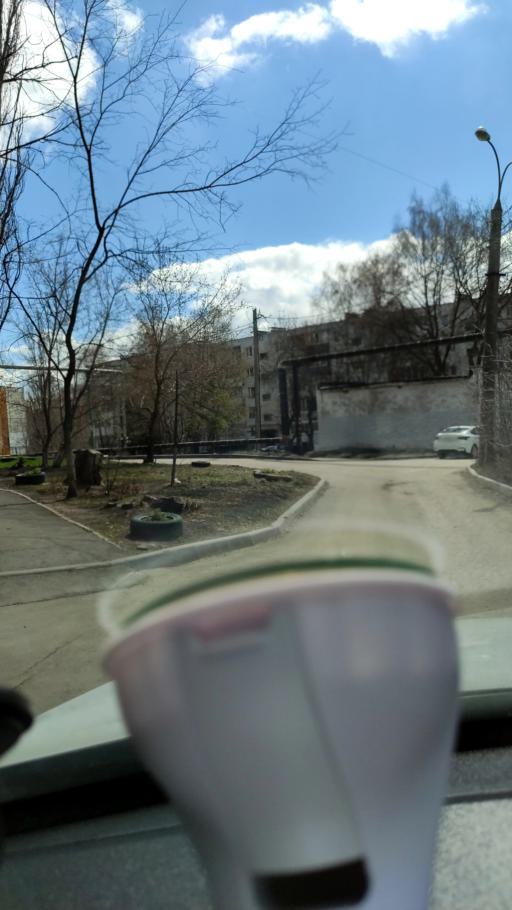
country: RU
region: Samara
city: Novosemeykino
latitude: 53.3428
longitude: 50.2250
